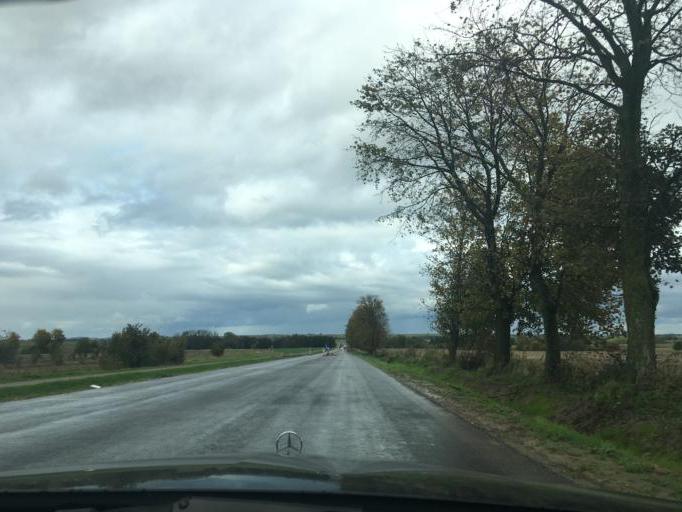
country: PL
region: Lublin Voivodeship
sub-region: Powiat lubelski
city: Wysokie
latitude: 50.9324
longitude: 22.6720
